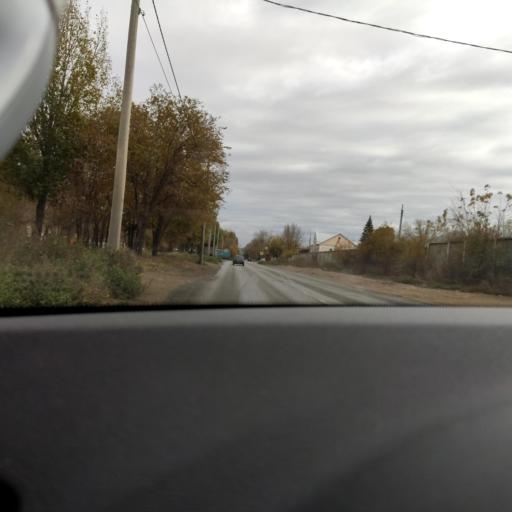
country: RU
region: Samara
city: Petra-Dubrava
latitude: 53.2451
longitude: 50.3087
